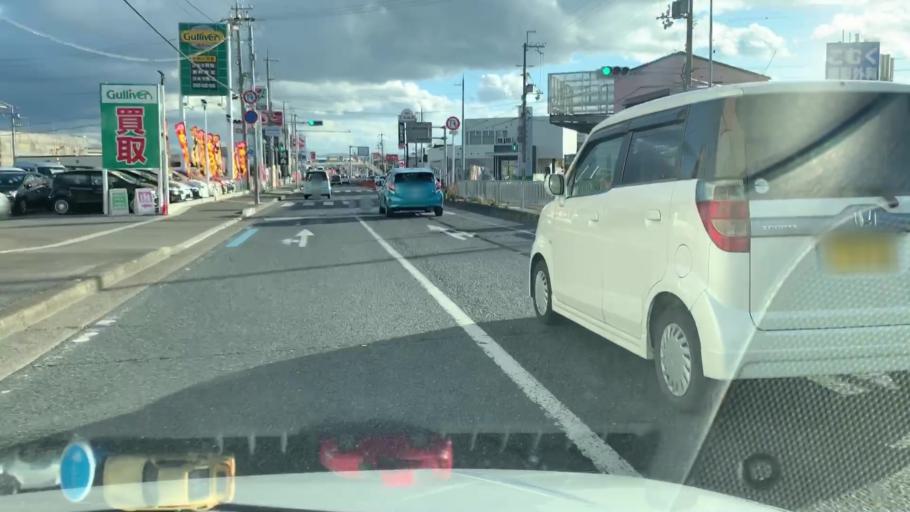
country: JP
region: Wakayama
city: Wakayama-shi
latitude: 34.2464
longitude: 135.1505
